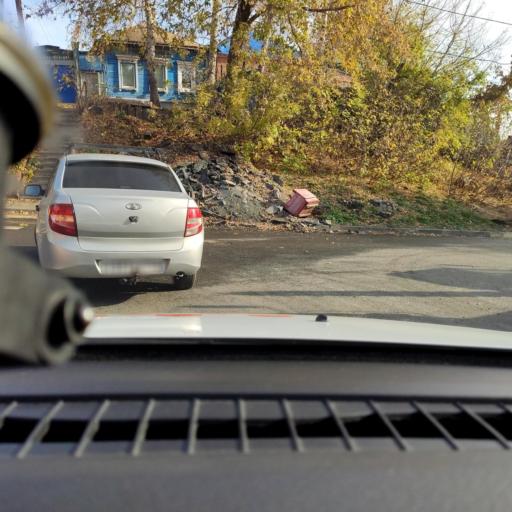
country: RU
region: Samara
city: Samara
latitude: 53.1806
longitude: 50.0968
